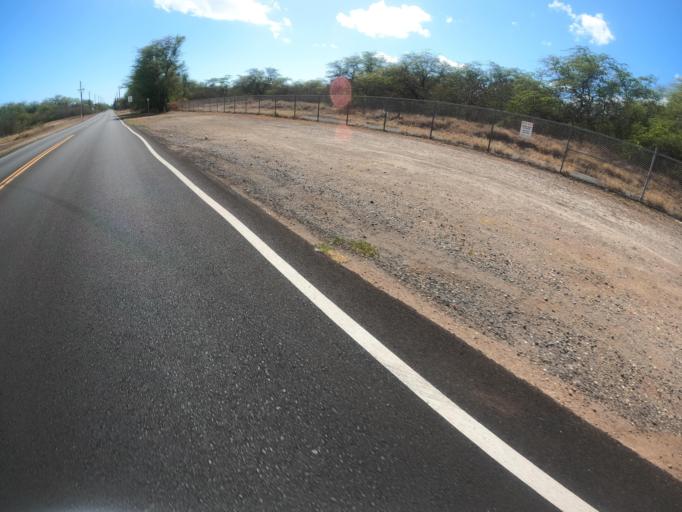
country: US
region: Hawaii
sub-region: Honolulu County
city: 'Ewa Villages
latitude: 21.3135
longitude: -158.0555
